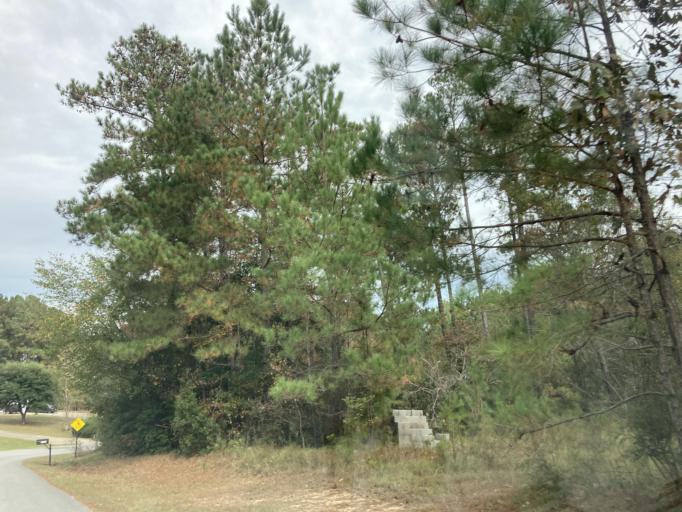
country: US
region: Mississippi
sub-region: Lamar County
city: Arnold Line
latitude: 31.3319
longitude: -89.4087
